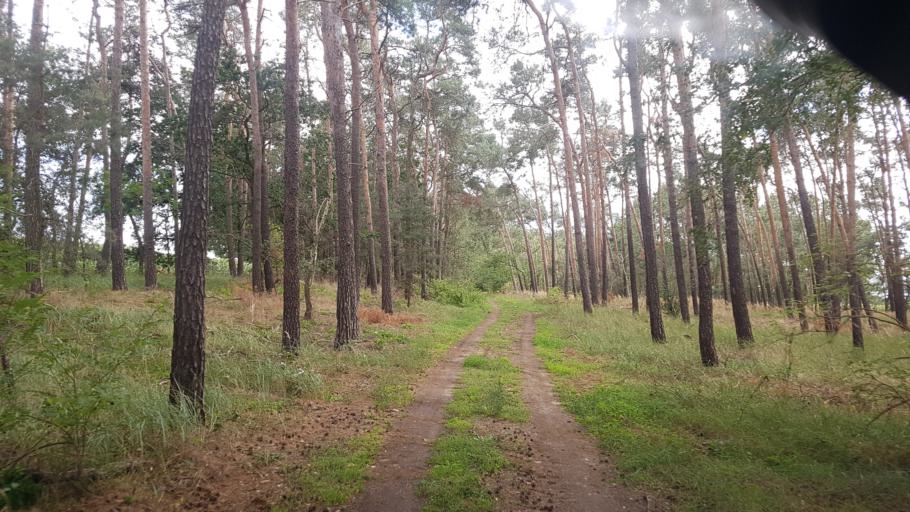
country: DE
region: Brandenburg
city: Schonewalde
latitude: 51.6774
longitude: 13.6256
